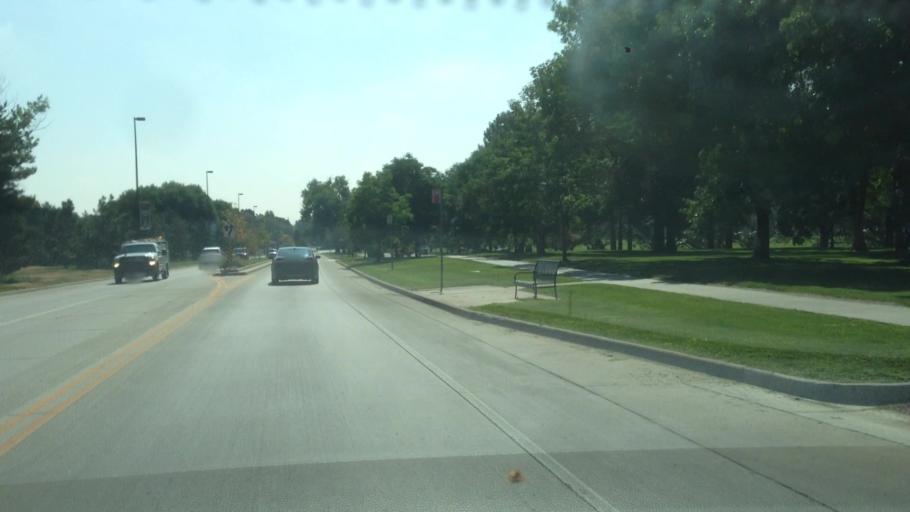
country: US
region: Colorado
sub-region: Denver County
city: Denver
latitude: 39.7512
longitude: -104.9457
